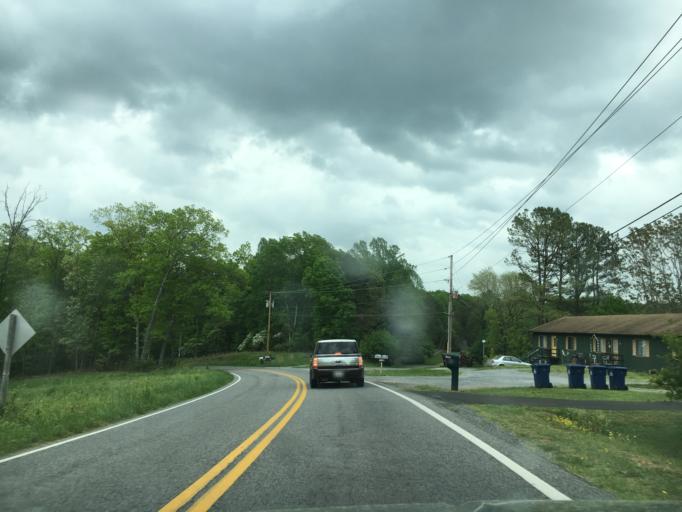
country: US
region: Virginia
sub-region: Campbell County
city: Rustburg
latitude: 37.3218
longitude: -79.1303
